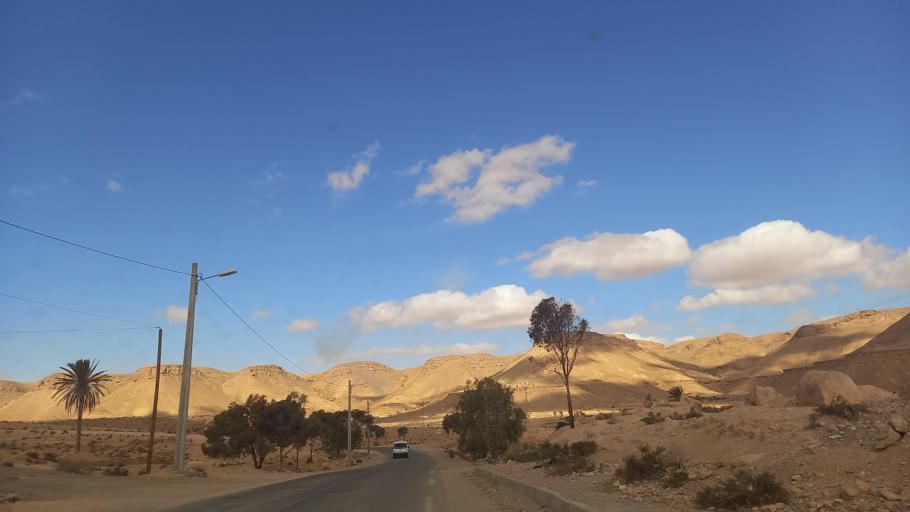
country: TN
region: Tataouine
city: Tataouine
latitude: 32.9153
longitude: 10.2773
